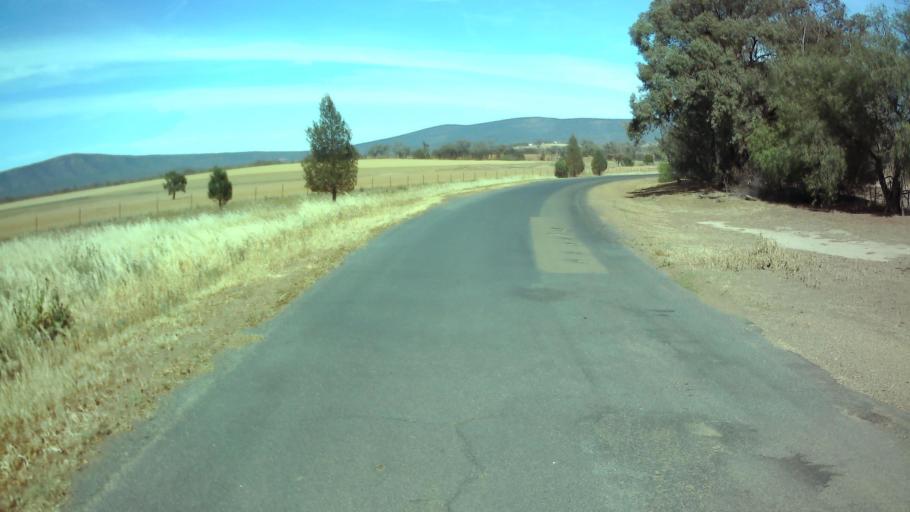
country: AU
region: New South Wales
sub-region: Weddin
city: Grenfell
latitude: -33.9314
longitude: 148.0927
